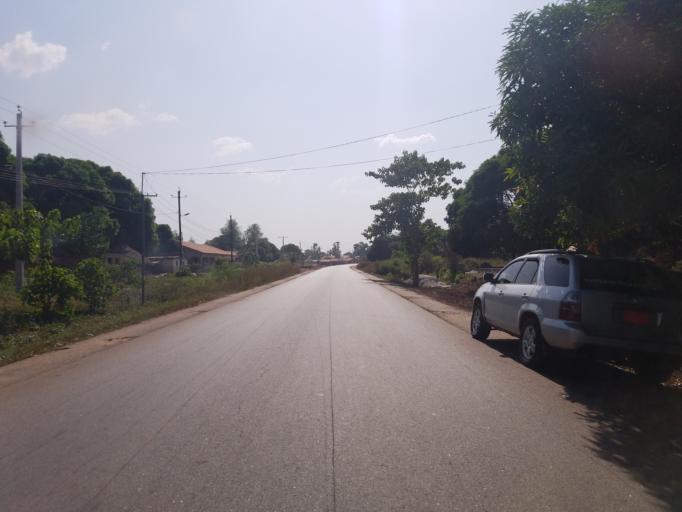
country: GN
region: Boke
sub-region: Fria
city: Fria
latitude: 10.0772
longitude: -13.7012
